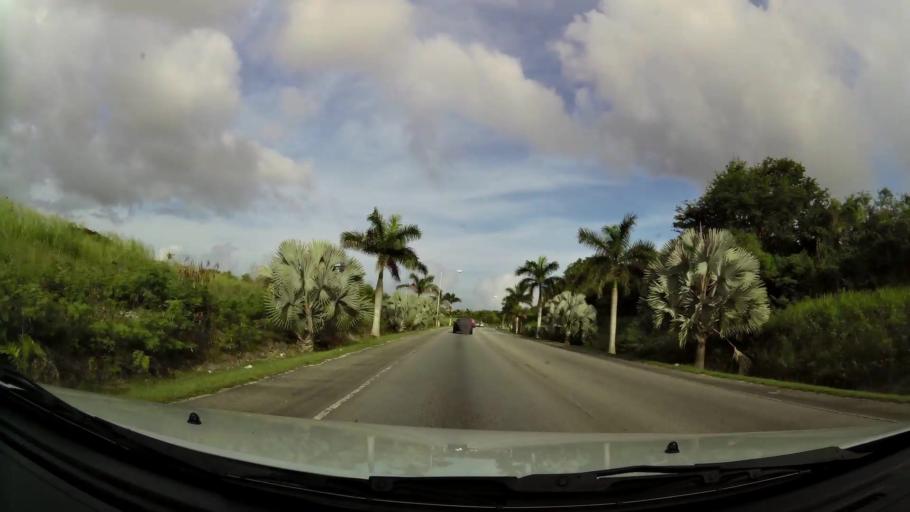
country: BB
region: Christ Church
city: Oistins
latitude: 13.0829
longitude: -59.5398
